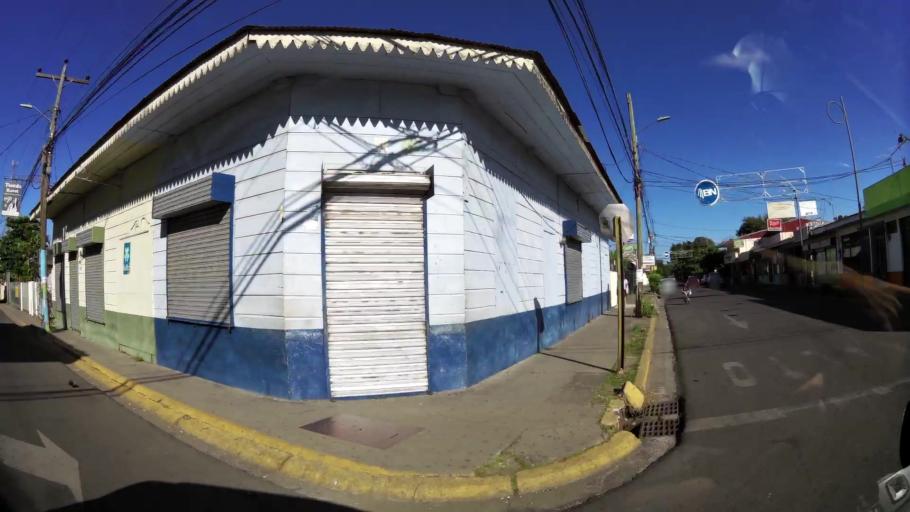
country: CR
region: Guanacaste
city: Belen
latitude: 10.4455
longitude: -85.5512
